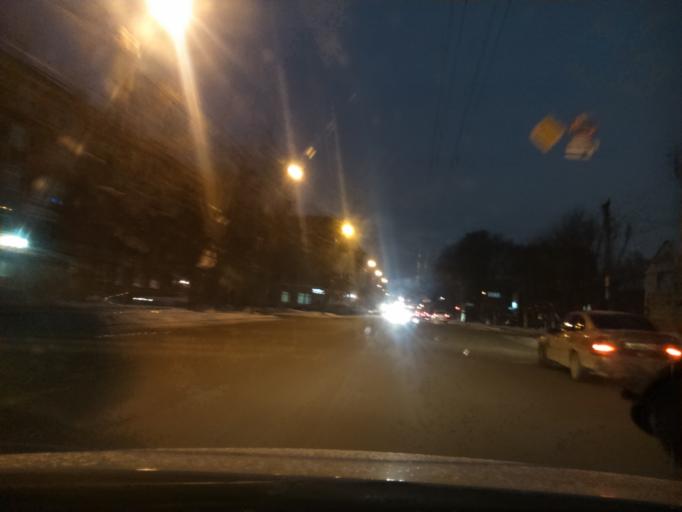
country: RU
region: Perm
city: Perm
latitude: 57.9865
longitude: 56.2488
